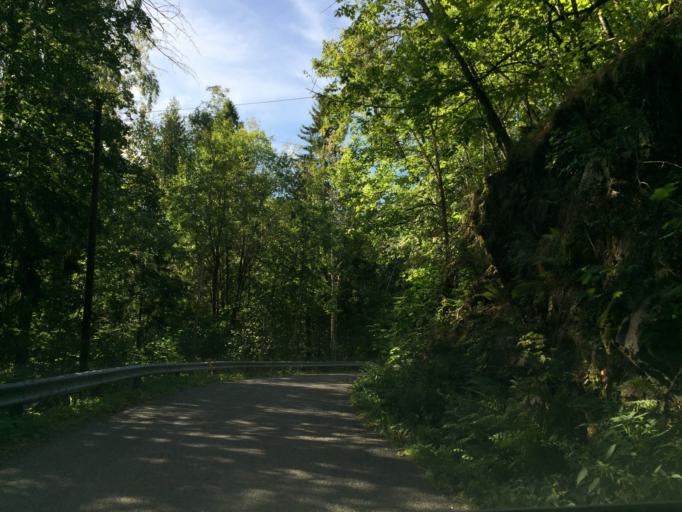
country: NO
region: Vestfold
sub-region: Hof
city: Hof
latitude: 59.4844
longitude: 10.1506
